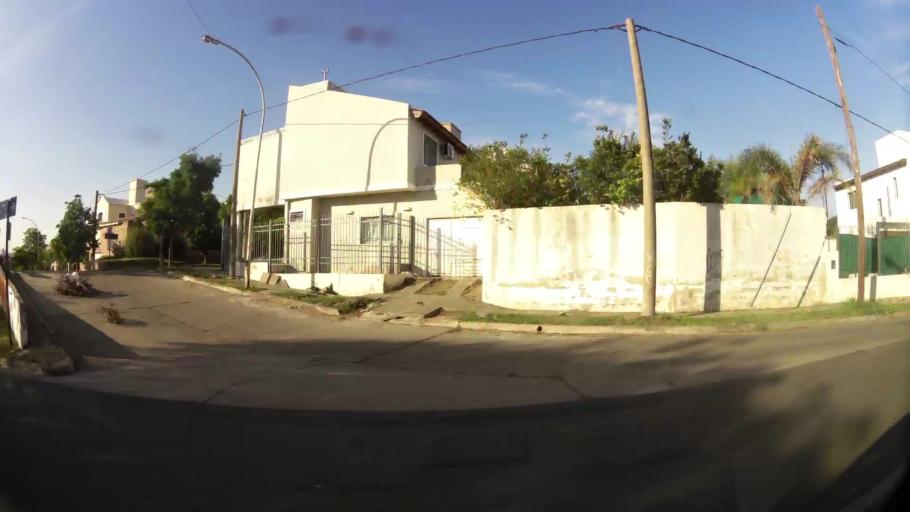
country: AR
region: Cordoba
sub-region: Departamento de Capital
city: Cordoba
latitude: -31.3885
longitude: -64.2371
